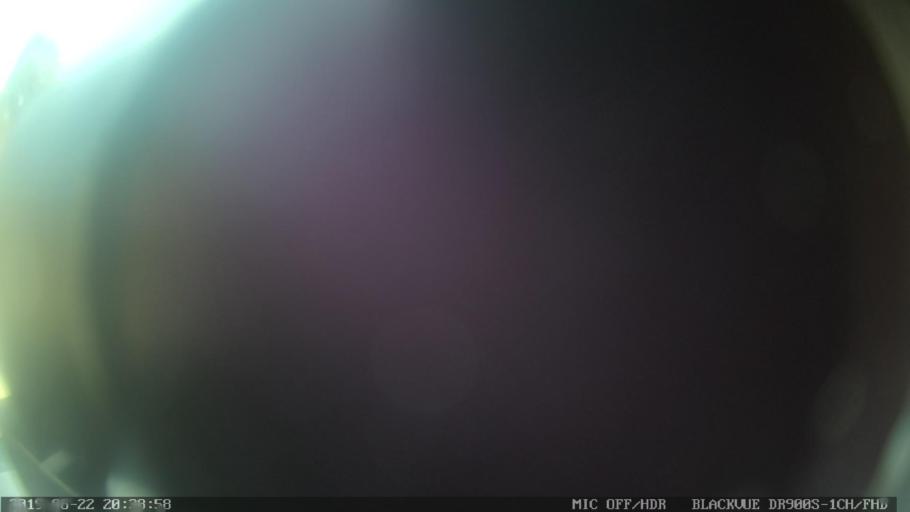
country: PT
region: Castelo Branco
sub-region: Proenca-A-Nova
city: Proenca-a-Nova
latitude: 39.6878
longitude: -7.7592
